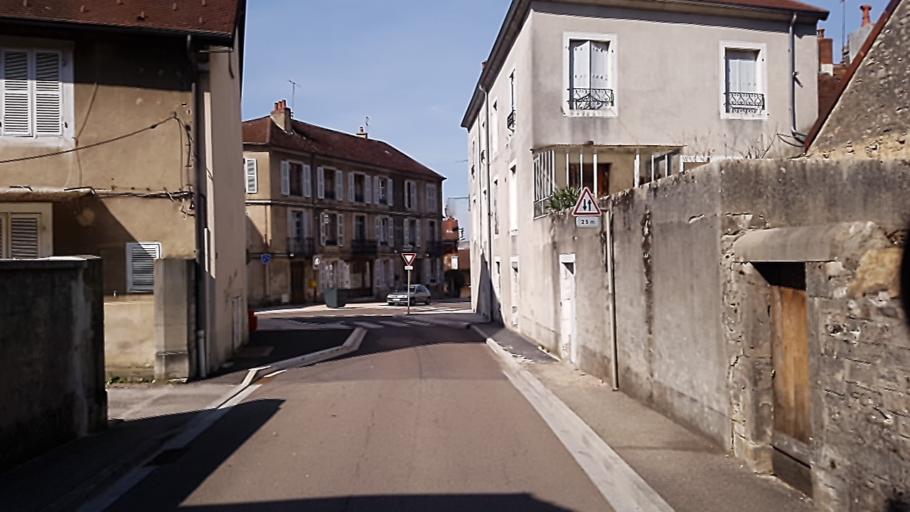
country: FR
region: Franche-Comte
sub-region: Departement du Jura
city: Poligny
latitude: 46.8391
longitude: 5.7099
